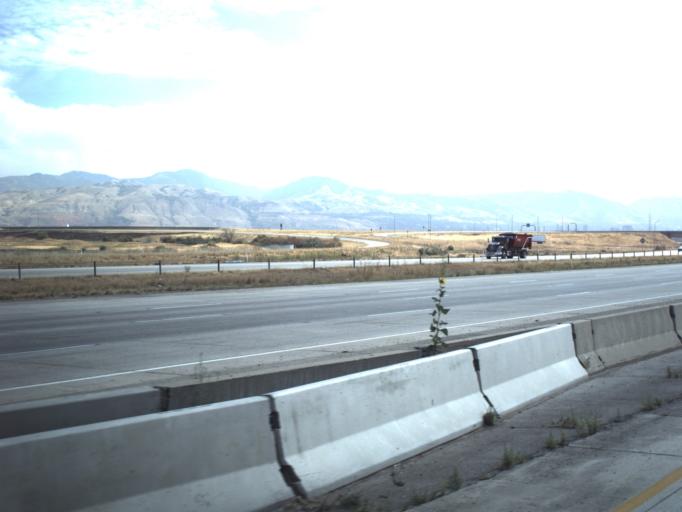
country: US
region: Utah
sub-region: Salt Lake County
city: West Valley City
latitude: 40.7654
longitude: -111.9941
